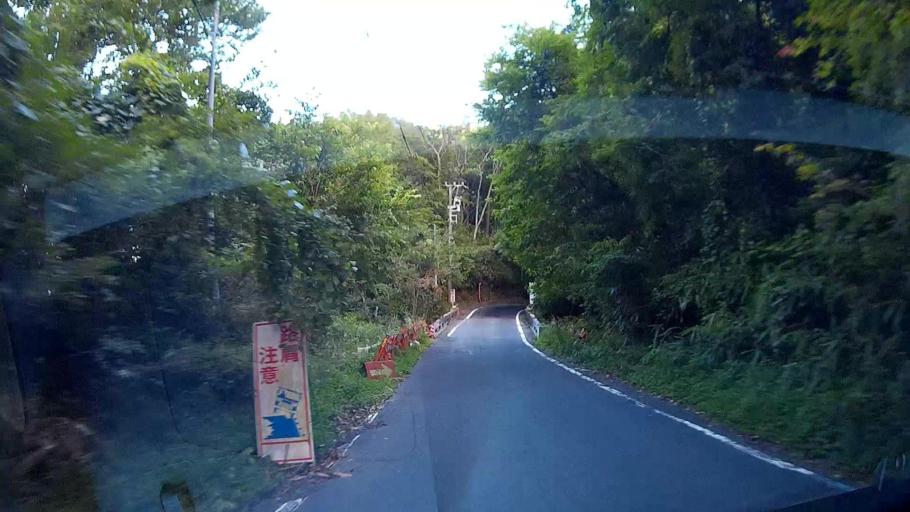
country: JP
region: Shizuoka
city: Shizuoka-shi
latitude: 35.1386
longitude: 138.2691
